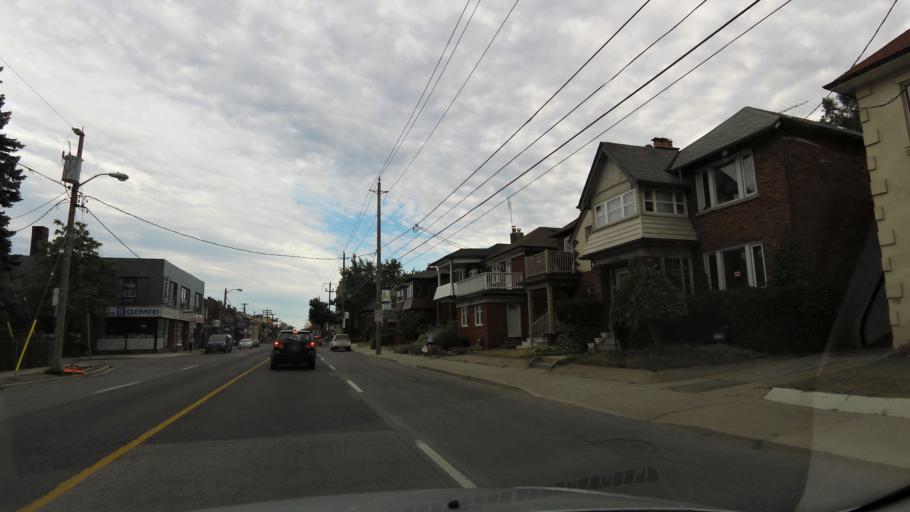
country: CA
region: Ontario
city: Etobicoke
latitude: 43.6595
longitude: -79.4887
